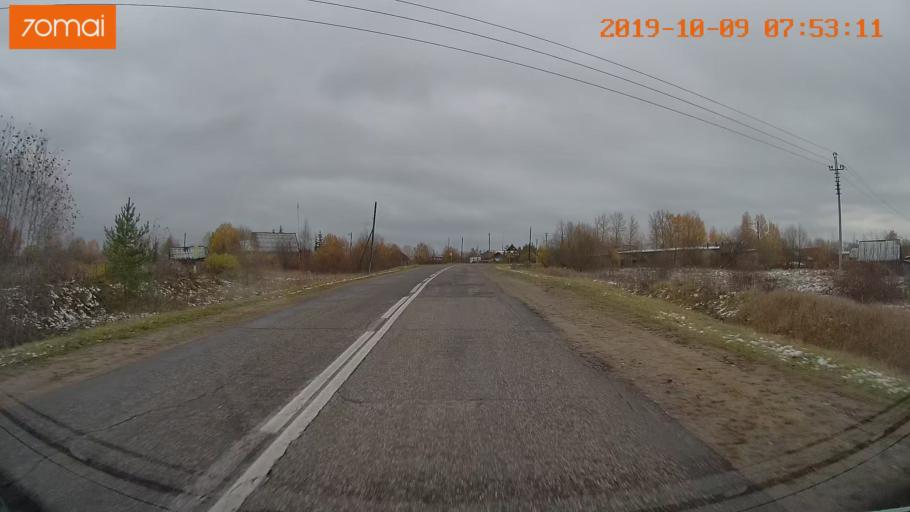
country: RU
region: Jaroslavl
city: Kukoboy
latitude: 58.6969
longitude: 39.8930
